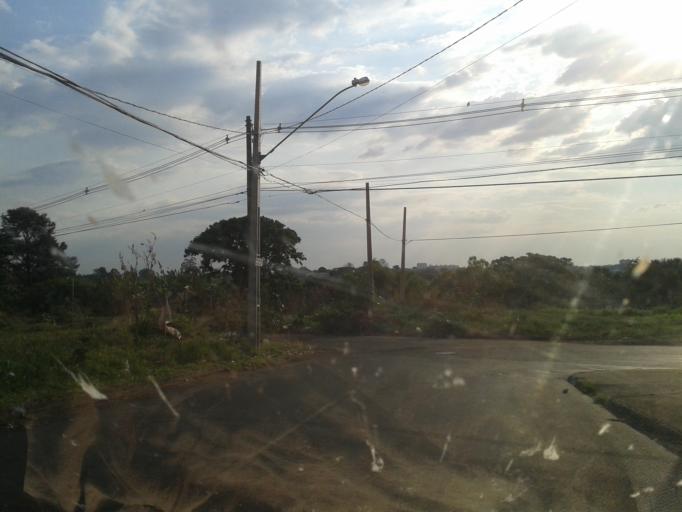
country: BR
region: Minas Gerais
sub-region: Uberlandia
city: Uberlandia
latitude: -18.9393
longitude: -48.3204
